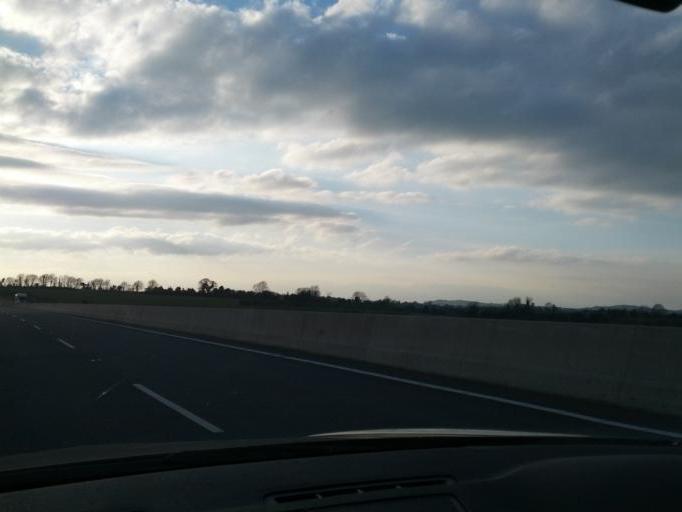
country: IE
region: Munster
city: Nenagh Bridge
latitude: 52.8744
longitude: -8.0352
